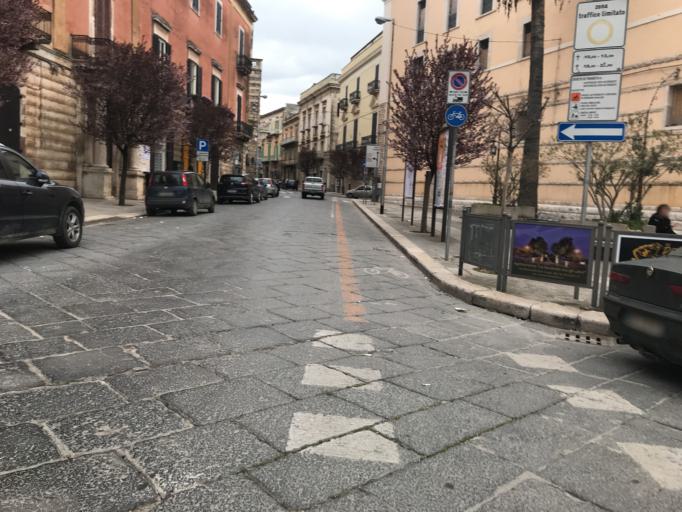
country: IT
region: Apulia
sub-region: Provincia di Bari
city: Corato
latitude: 41.1539
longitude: 16.4098
